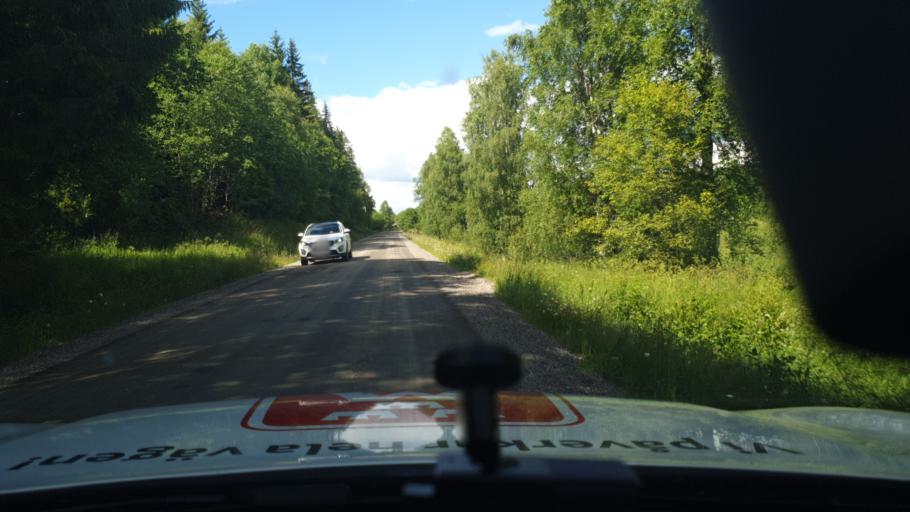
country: SE
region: Vaermland
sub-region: Hagfors Kommun
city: Ekshaerad
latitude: 60.4240
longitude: 13.2441
